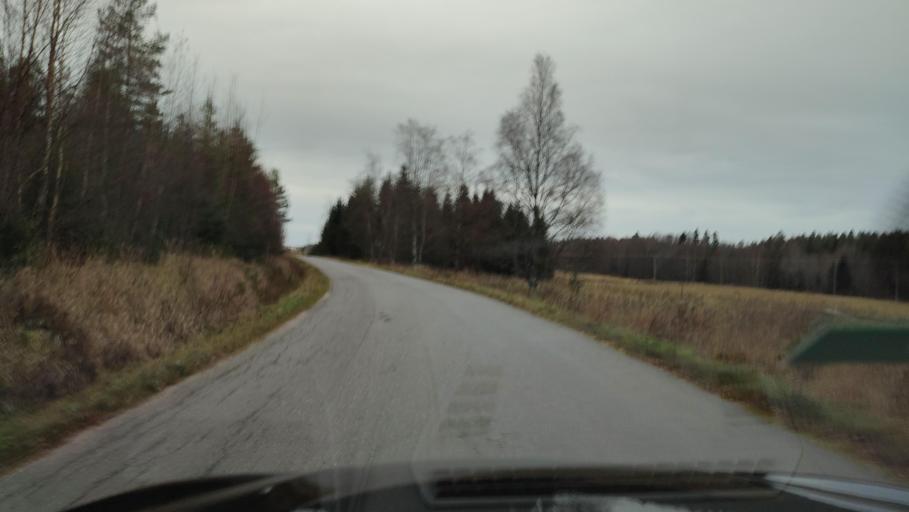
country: FI
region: Ostrobothnia
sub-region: Sydosterbotten
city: Naerpes
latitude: 62.4208
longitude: 21.4055
